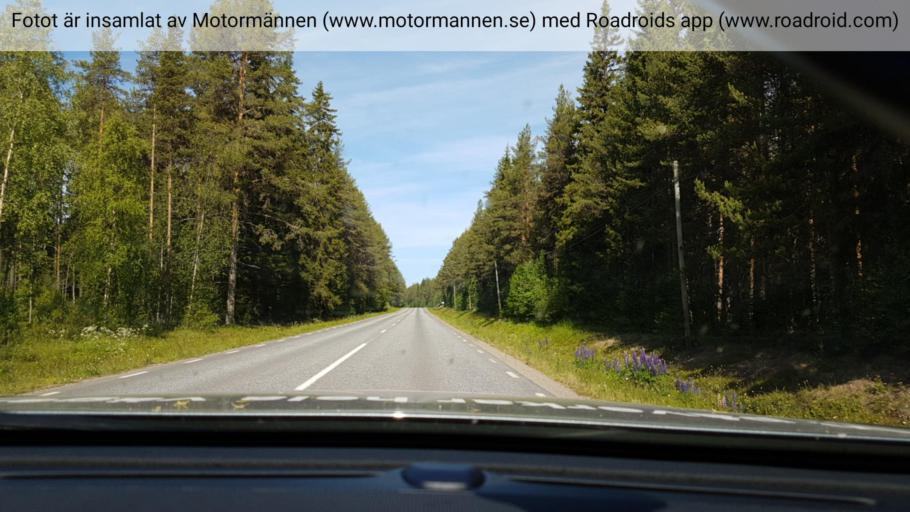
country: SE
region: Vaesterbotten
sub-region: Dorotea Kommun
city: Dorotea
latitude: 64.2605
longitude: 16.3735
